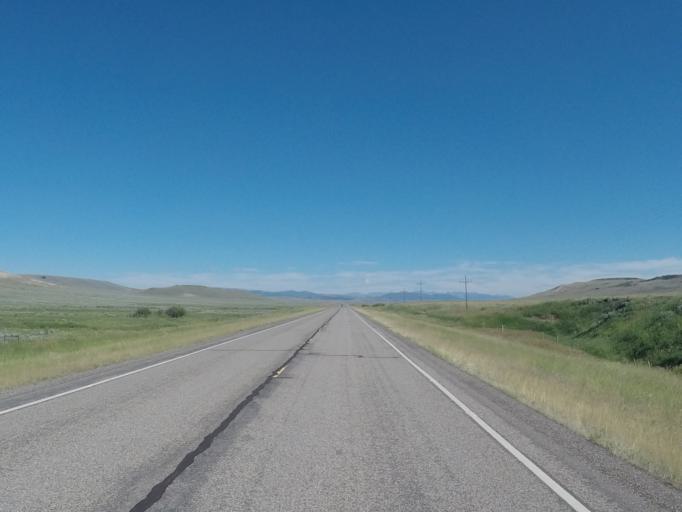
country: US
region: Montana
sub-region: Meagher County
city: White Sulphur Springs
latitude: 46.3761
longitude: -110.8535
